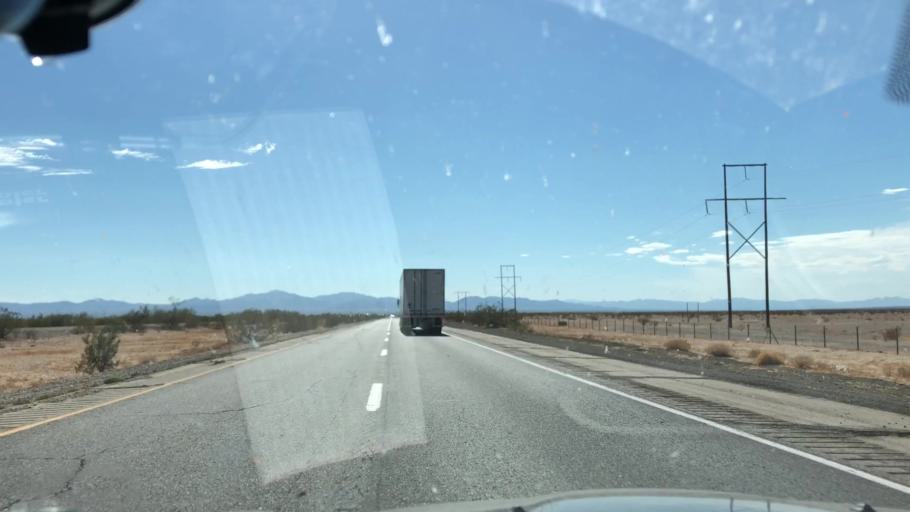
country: US
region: California
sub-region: Riverside County
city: Mesa Verde
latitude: 33.6063
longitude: -114.9426
